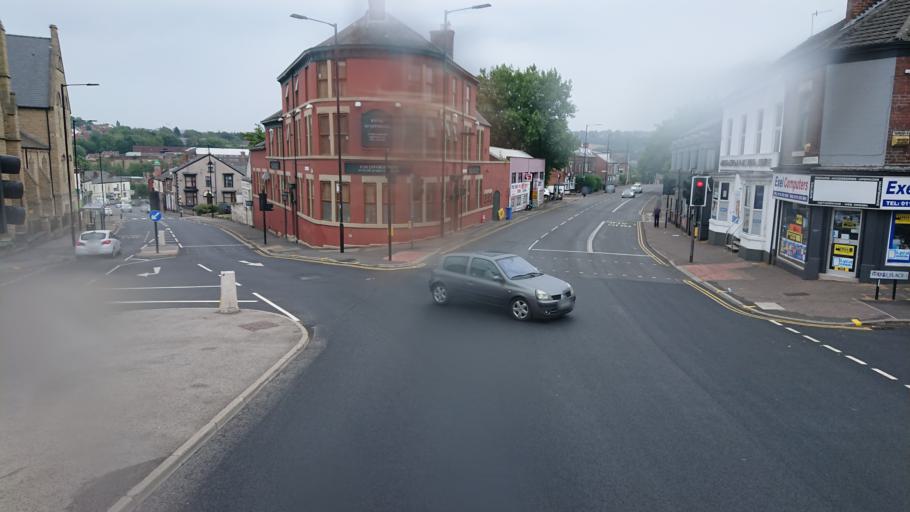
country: GB
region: England
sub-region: Sheffield
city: Sheffield
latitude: 53.3666
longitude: -1.4750
